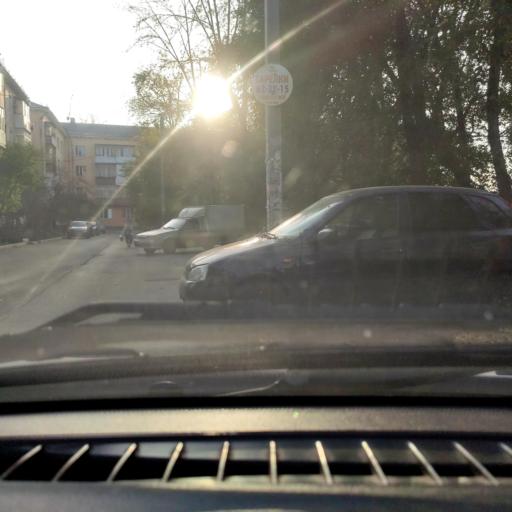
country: RU
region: Samara
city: Tol'yatti
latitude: 53.5161
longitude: 49.4138
